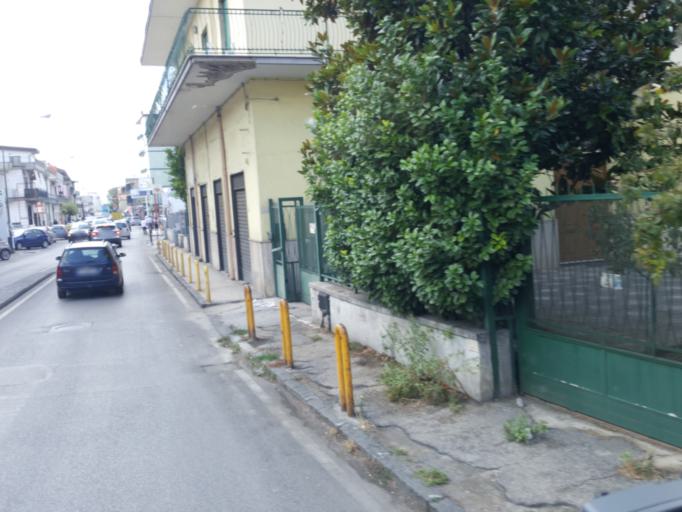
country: IT
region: Campania
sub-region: Provincia di Napoli
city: Nola
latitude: 40.9212
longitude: 14.5354
